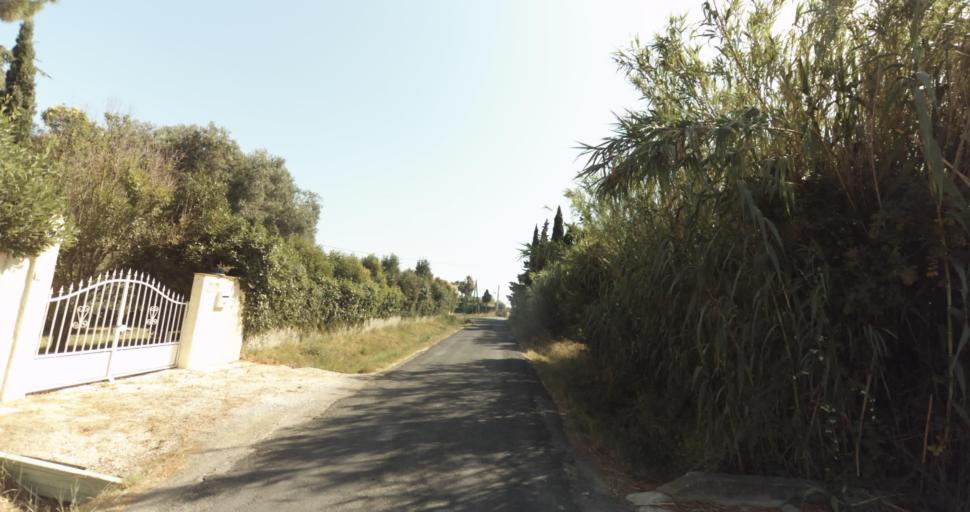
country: FR
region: Languedoc-Roussillon
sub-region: Departement des Pyrenees-Orientales
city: Alenya
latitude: 42.6362
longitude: 3.0046
